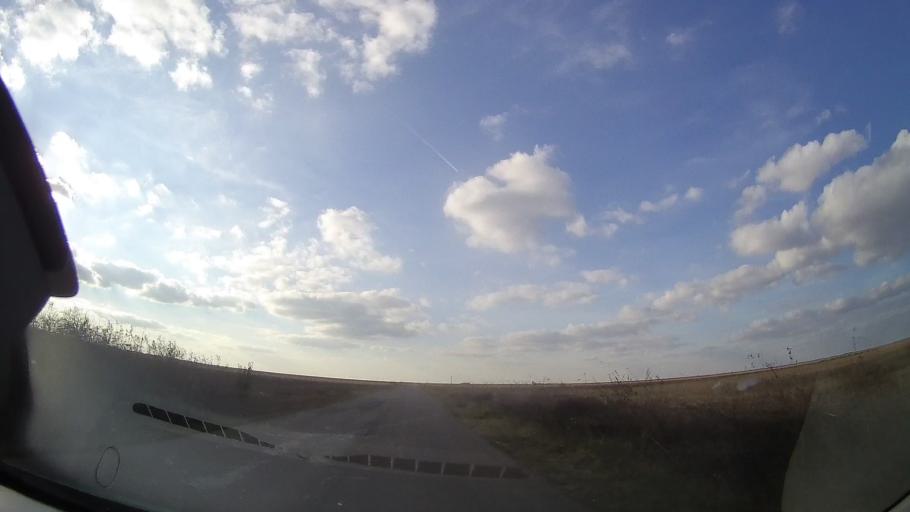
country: RO
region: Constanta
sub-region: Comuna Cerchezu
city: Cerchezu
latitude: 43.8244
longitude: 28.1394
